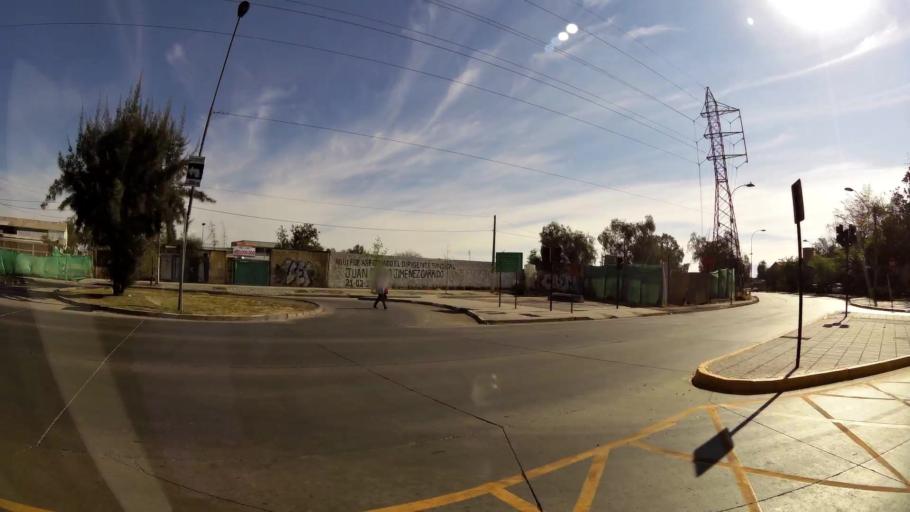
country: CL
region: Santiago Metropolitan
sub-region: Provincia de Santiago
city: Santiago
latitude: -33.4791
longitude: -70.6338
